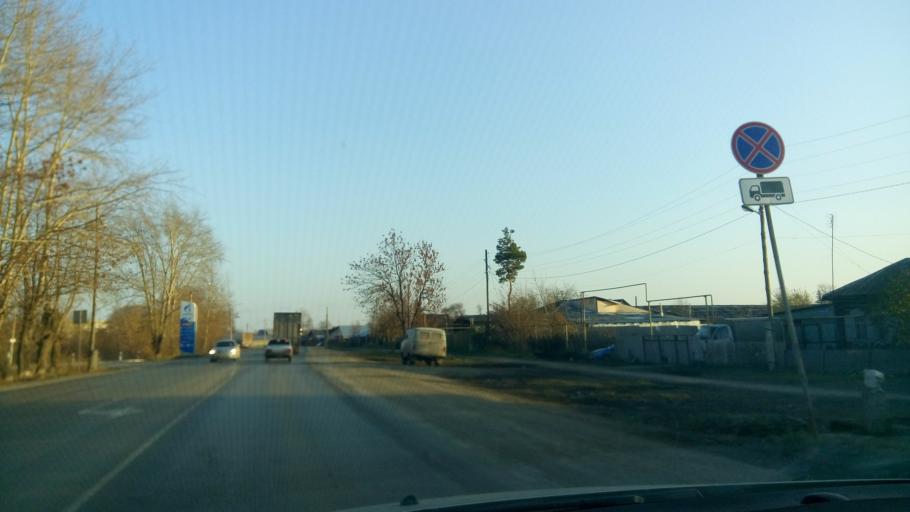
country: RU
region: Sverdlovsk
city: Bogdanovich
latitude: 56.7746
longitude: 62.0347
